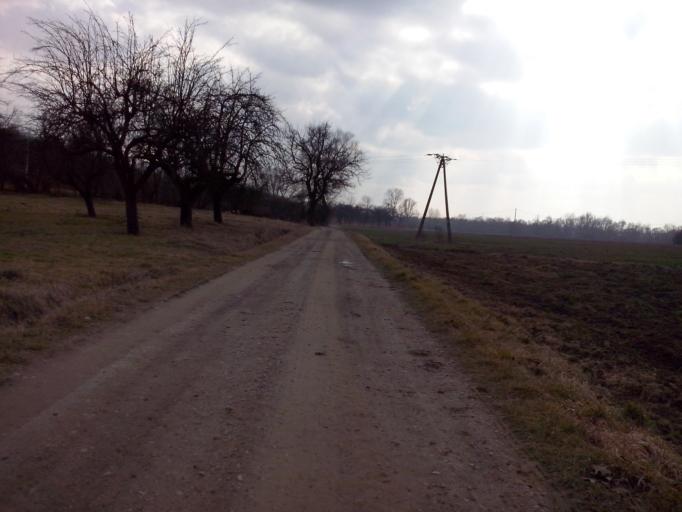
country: PL
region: Subcarpathian Voivodeship
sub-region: Powiat nizanski
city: Krzeszow
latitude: 50.4150
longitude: 22.3262
